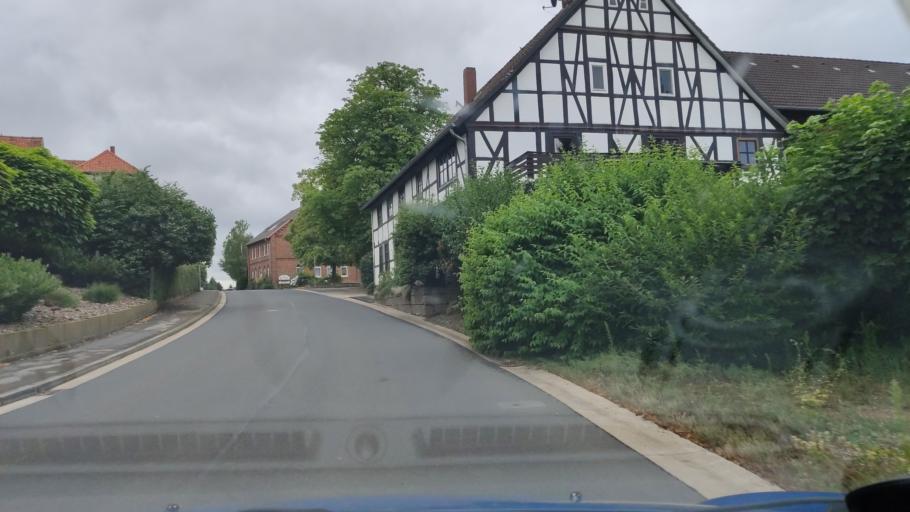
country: DE
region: Lower Saxony
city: Coppenbrugge
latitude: 52.1042
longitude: 9.5018
